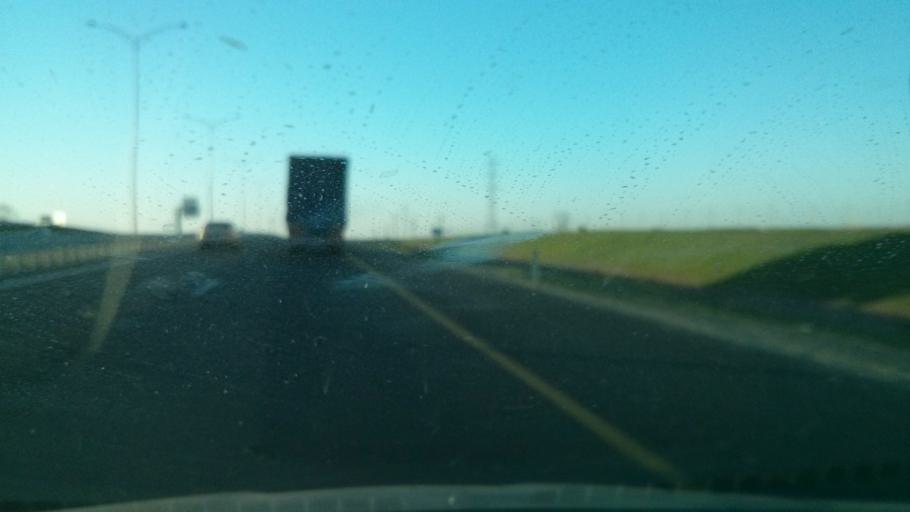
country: IL
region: Southern District
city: Lehavim
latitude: 31.4293
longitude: 34.7806
